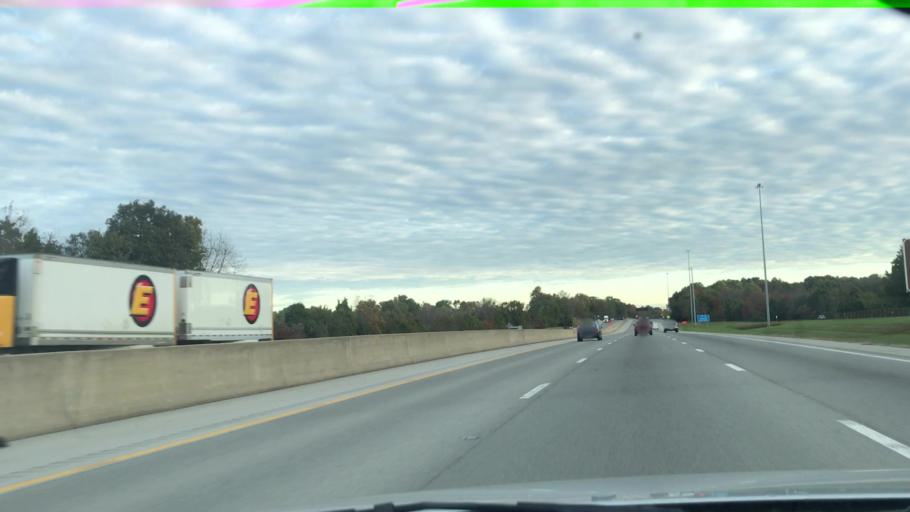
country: US
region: Kentucky
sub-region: Simpson County
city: Franklin
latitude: 36.6427
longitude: -86.5700
